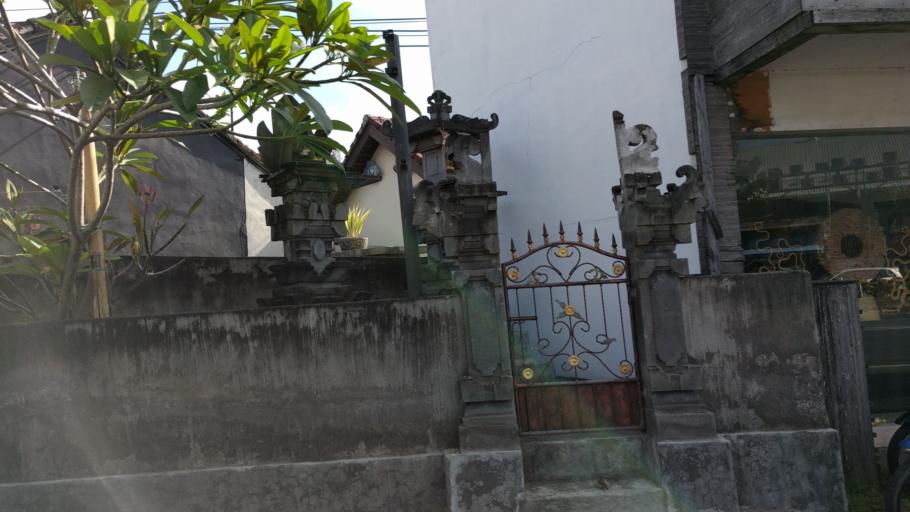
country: ID
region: Bali
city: Kuta
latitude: -8.6816
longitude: 115.1647
